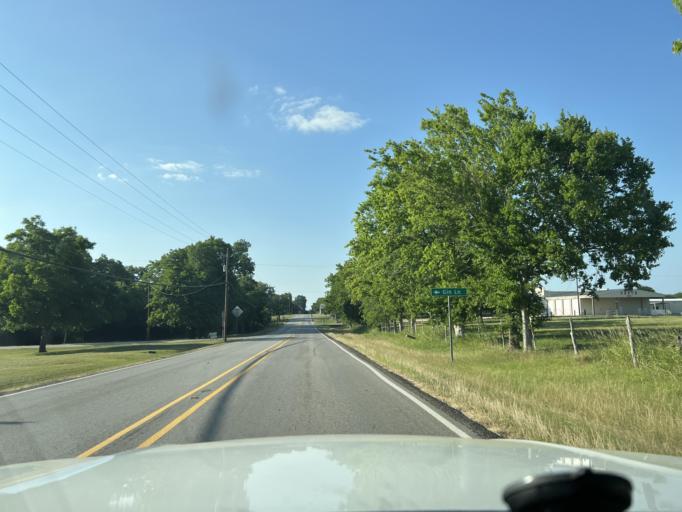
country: US
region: Texas
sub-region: Washington County
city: Brenham
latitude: 30.1376
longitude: -96.2571
